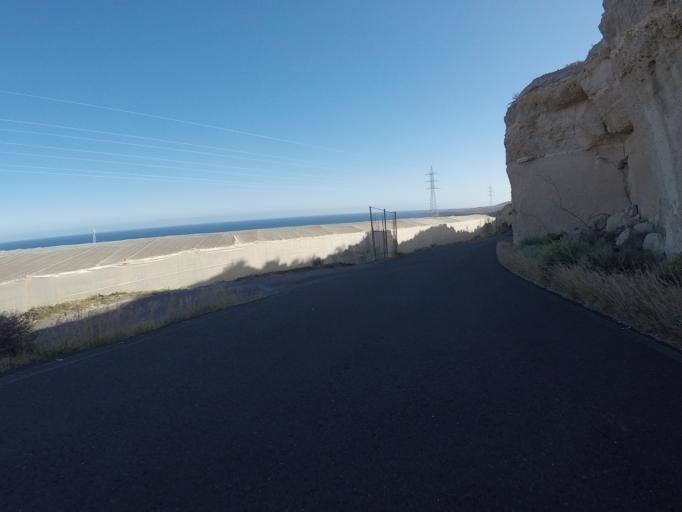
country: ES
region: Canary Islands
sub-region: Provincia de Santa Cruz de Tenerife
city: Fasnia
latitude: 28.2315
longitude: -16.4146
